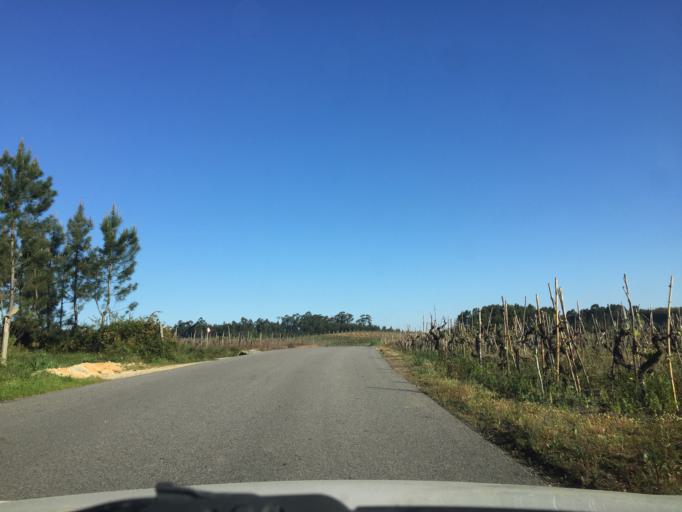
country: PT
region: Aveiro
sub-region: Anadia
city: Sangalhos
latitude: 40.4581
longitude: -8.4919
